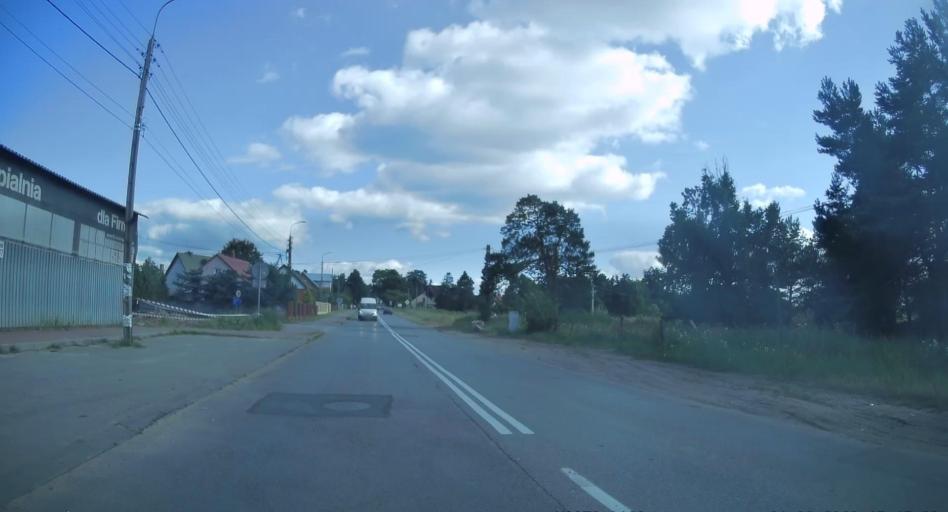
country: PL
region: Swietokrzyskie
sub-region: Powiat skarzyski
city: Suchedniow
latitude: 51.0344
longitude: 20.8381
